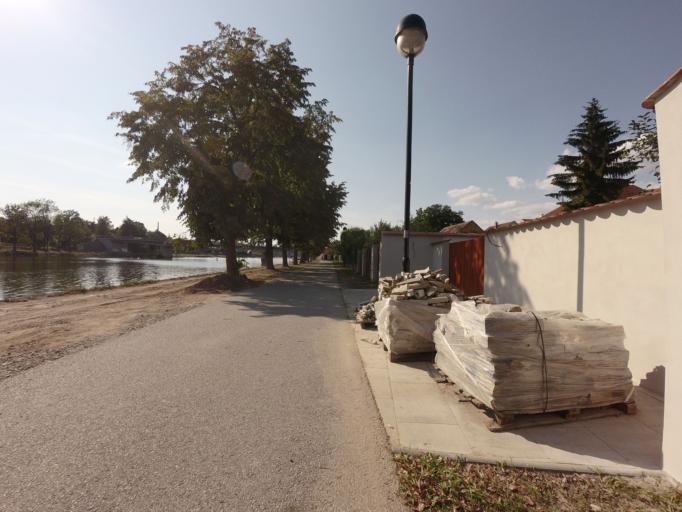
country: CZ
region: Jihocesky
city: Tyn nad Vltavou
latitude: 49.2208
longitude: 14.4236
